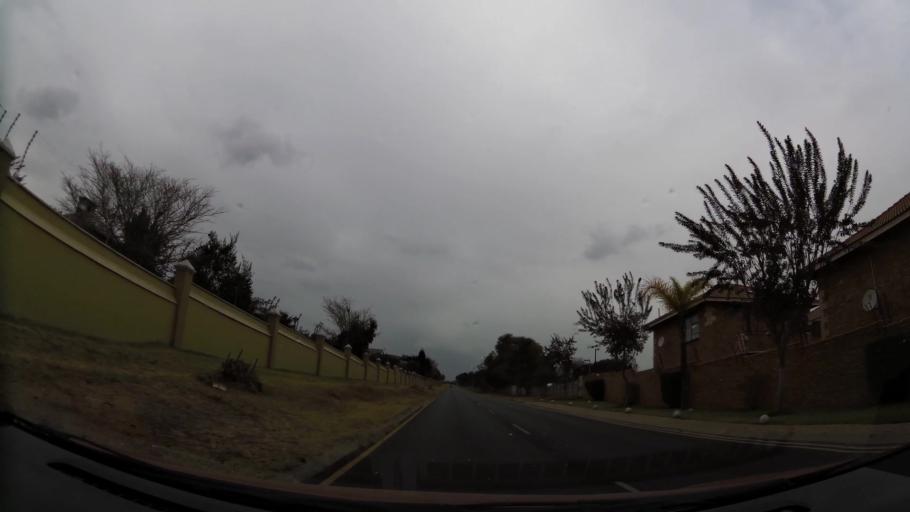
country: ZA
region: Gauteng
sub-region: City of Johannesburg Metropolitan Municipality
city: Roodepoort
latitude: -26.0940
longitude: 27.9155
